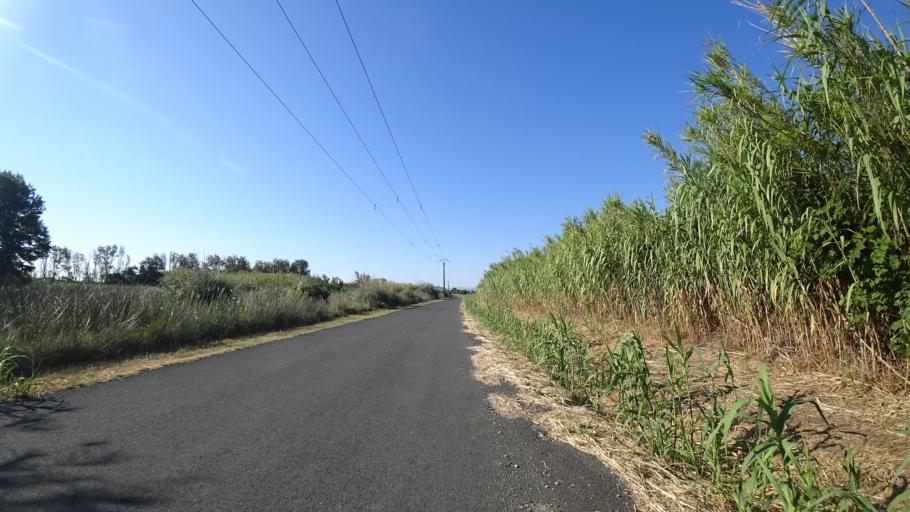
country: FR
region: Languedoc-Roussillon
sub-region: Departement des Pyrenees-Orientales
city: Le Barcares
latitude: 42.7682
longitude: 3.0183
